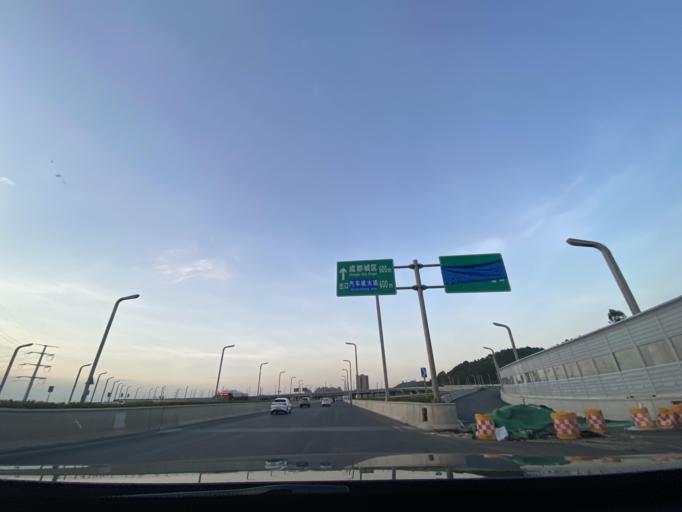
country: CN
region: Sichuan
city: Longquan
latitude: 30.5903
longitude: 104.3030
